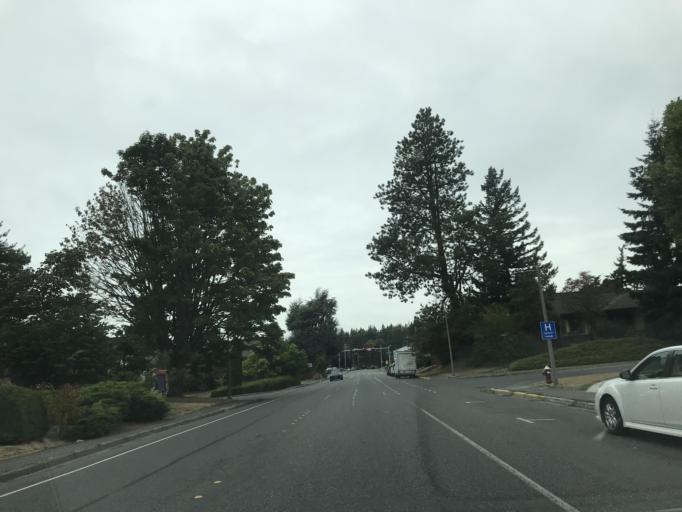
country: US
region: Washington
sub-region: Whatcom County
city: Bellingham
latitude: 48.7670
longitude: -122.4769
